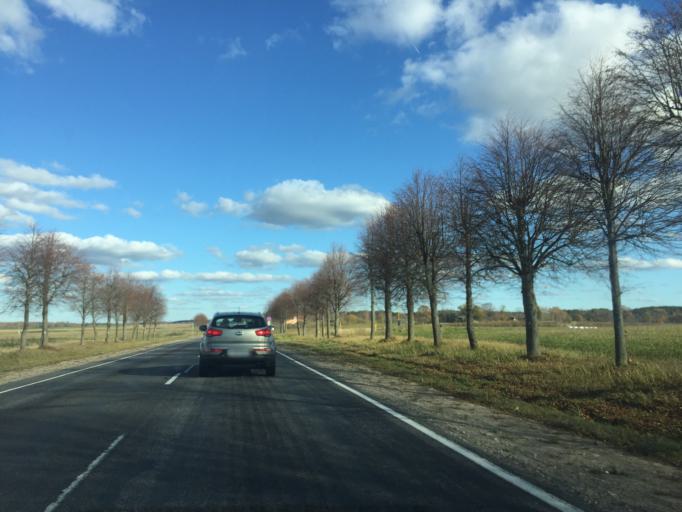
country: BY
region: Vitebsk
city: Pastavy
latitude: 55.0233
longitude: 26.9297
